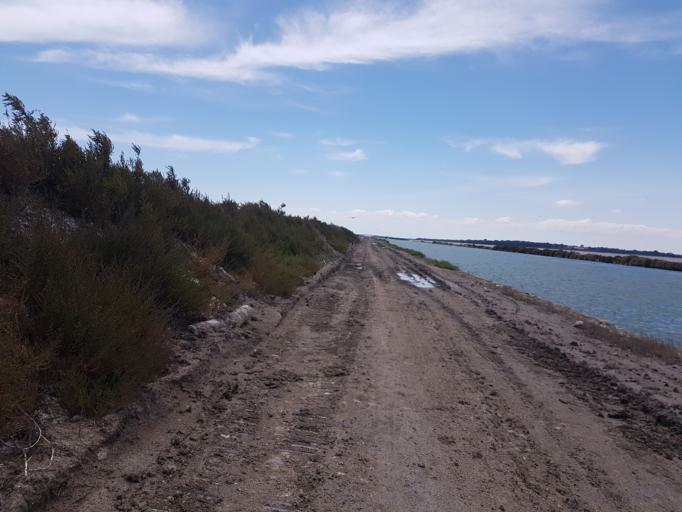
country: FR
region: Languedoc-Roussillon
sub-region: Departement de l'Herault
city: Vic-la-Gardiole
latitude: 43.4808
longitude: 3.8356
